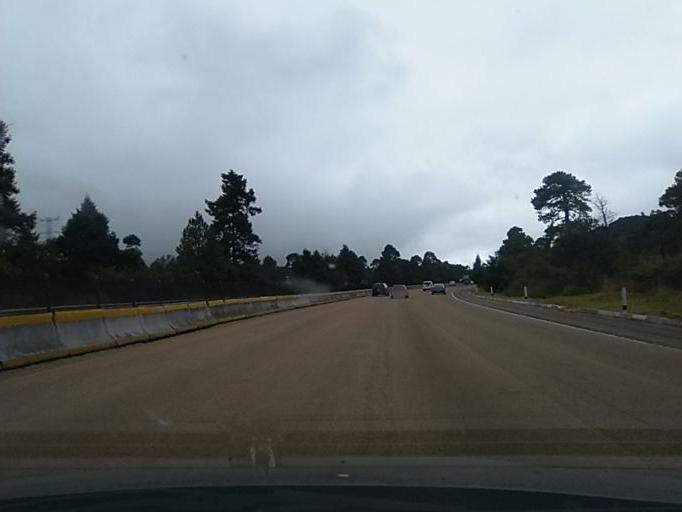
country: MX
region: Morelos
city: Tres Marias
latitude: 19.1146
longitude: -99.1829
